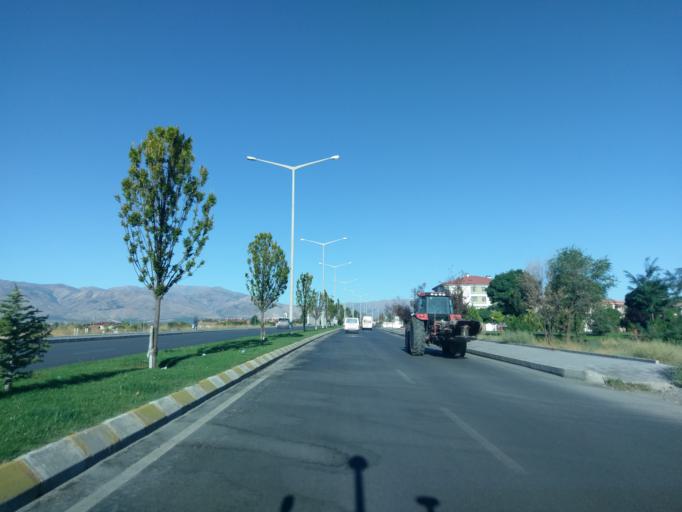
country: TR
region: Erzincan
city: Erzincan
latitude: 39.7489
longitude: 39.4633
